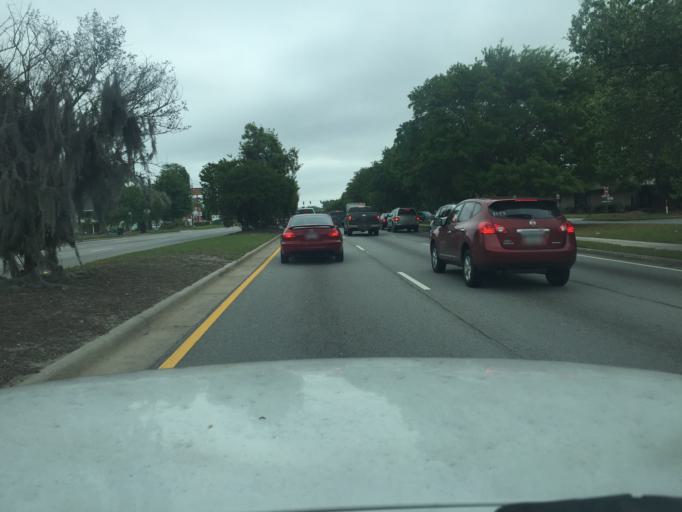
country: US
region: Georgia
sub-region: Chatham County
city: Montgomery
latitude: 31.9833
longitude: -81.1547
